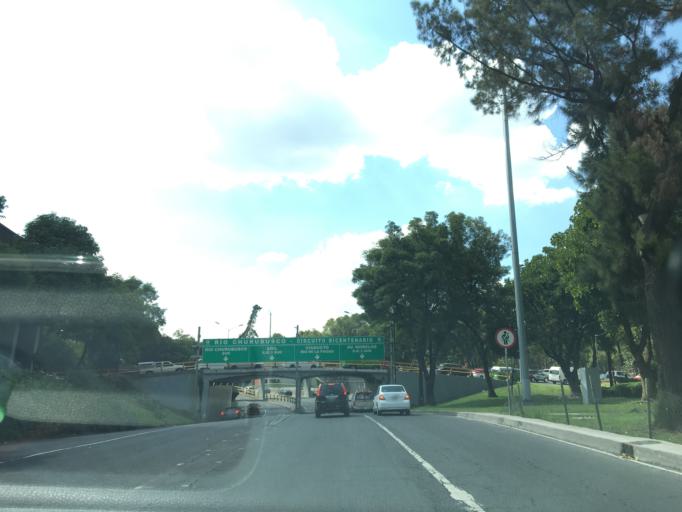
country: MX
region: Mexico City
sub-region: Iztacalco
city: Iztacalco
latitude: 19.4094
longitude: -99.0963
